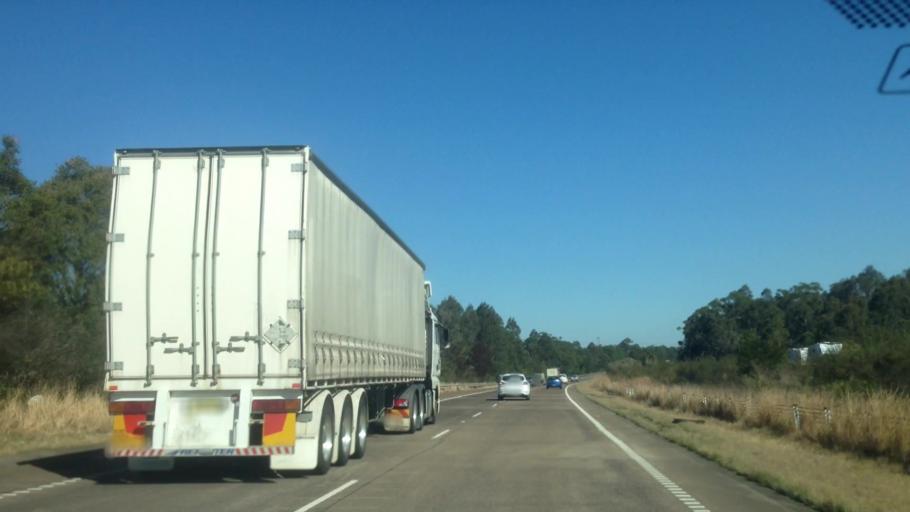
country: AU
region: New South Wales
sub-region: Wyong Shire
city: Charmhaven
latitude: -33.1826
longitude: 151.4679
